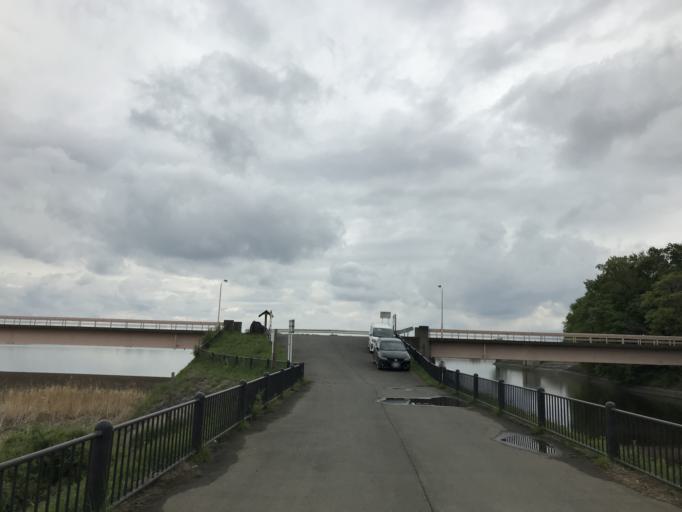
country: JP
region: Ibaraki
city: Mitsukaido
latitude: 36.0426
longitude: 140.0284
